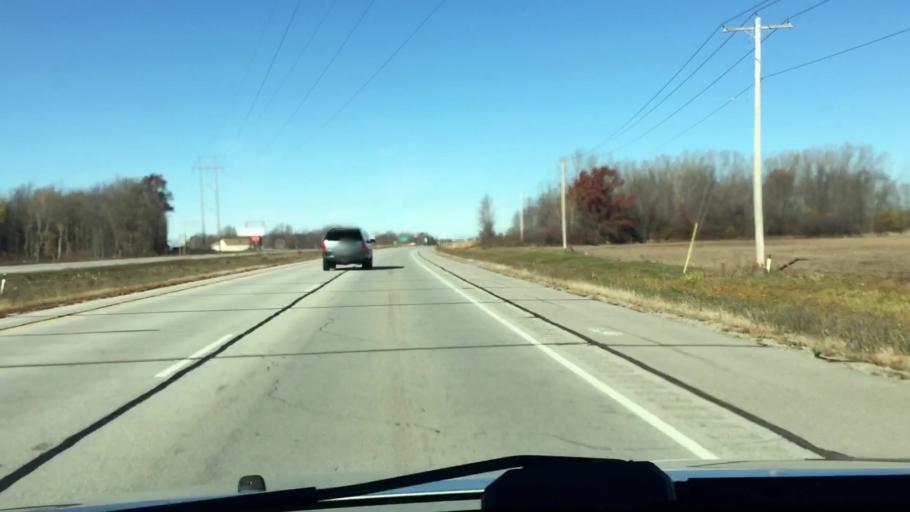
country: US
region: Wisconsin
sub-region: Brown County
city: Oneida
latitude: 44.5814
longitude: -88.1838
